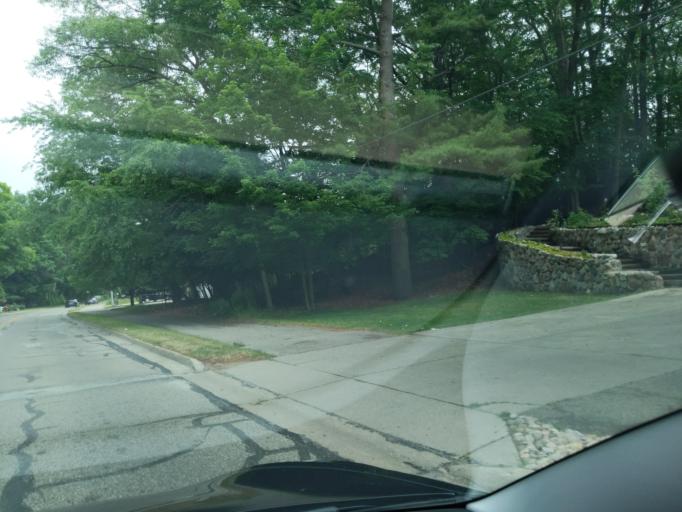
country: US
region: Michigan
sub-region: Muskegon County
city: Roosevelt Park
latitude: 43.2179
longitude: -86.3250
